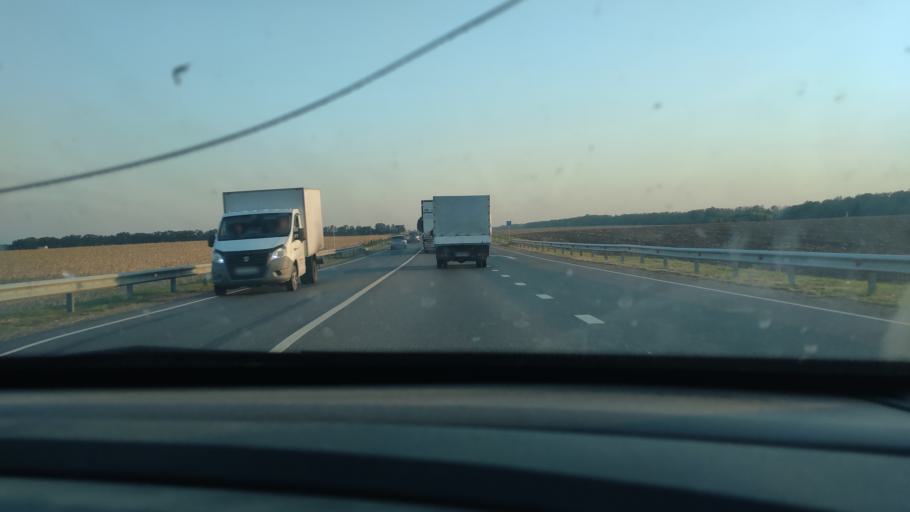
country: RU
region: Krasnodarskiy
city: Bryukhovetskaya
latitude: 45.7424
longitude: 38.9864
